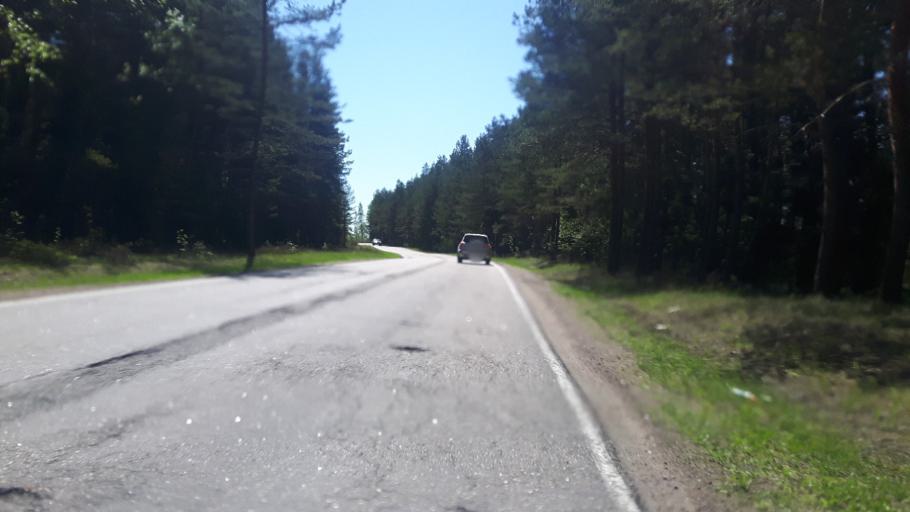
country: RU
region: Leningrad
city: Glebychevo
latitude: 60.3360
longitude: 28.8217
